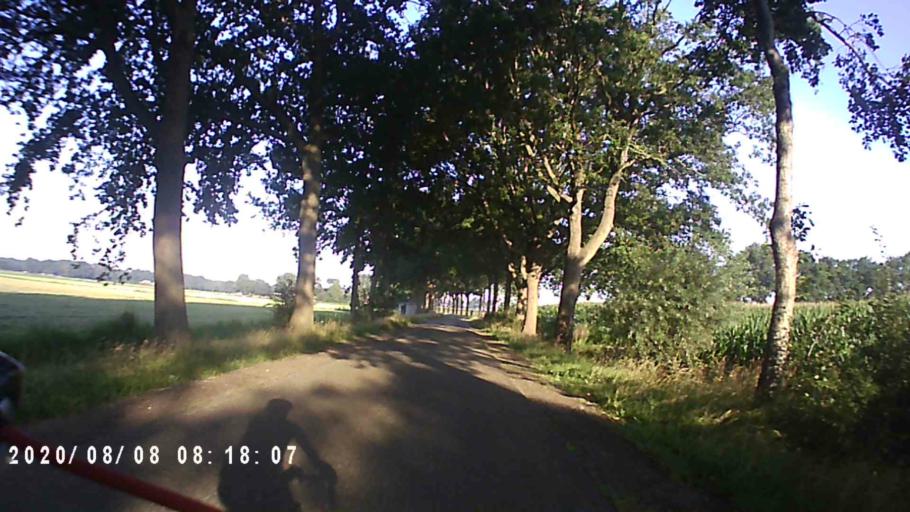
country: NL
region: Groningen
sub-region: Gemeente Leek
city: Leek
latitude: 53.0961
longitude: 6.3254
